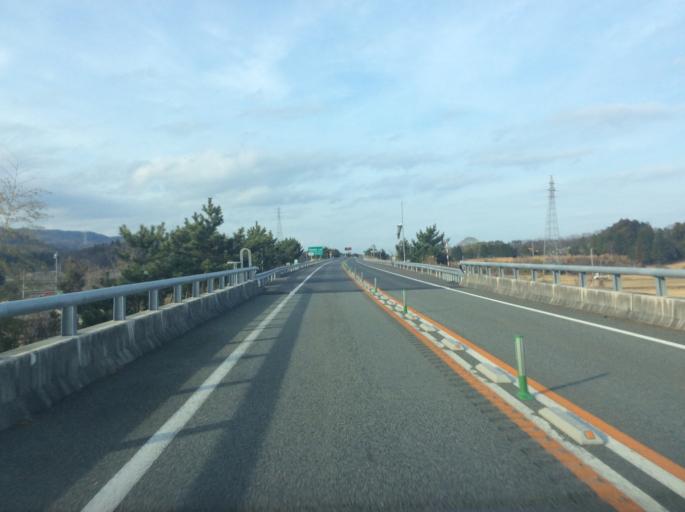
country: JP
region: Fukushima
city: Namie
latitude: 37.3670
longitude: 140.9679
